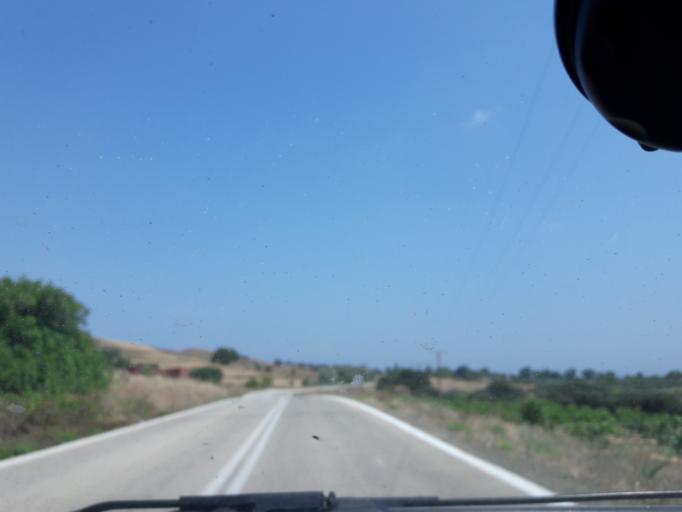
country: GR
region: North Aegean
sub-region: Nomos Lesvou
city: Myrina
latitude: 39.9253
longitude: 25.3222
